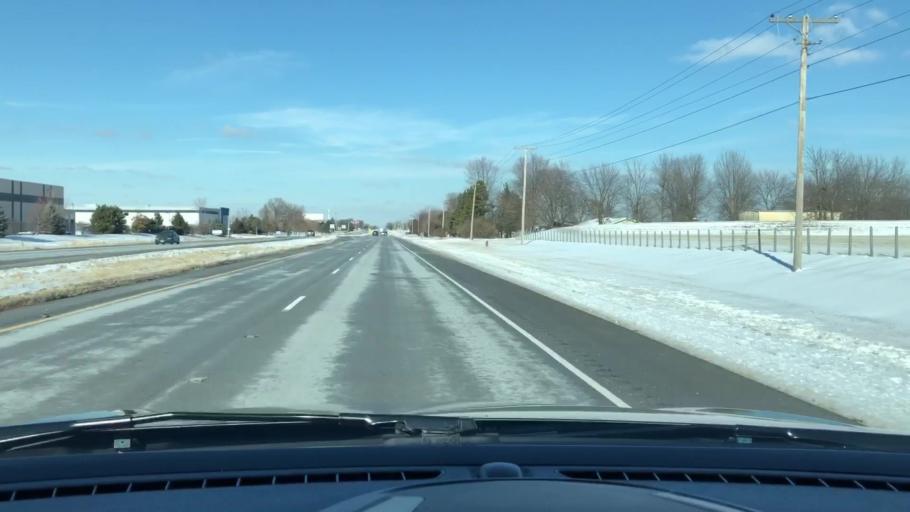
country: US
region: Illinois
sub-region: Will County
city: Preston Heights
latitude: 41.4603
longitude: -88.0793
